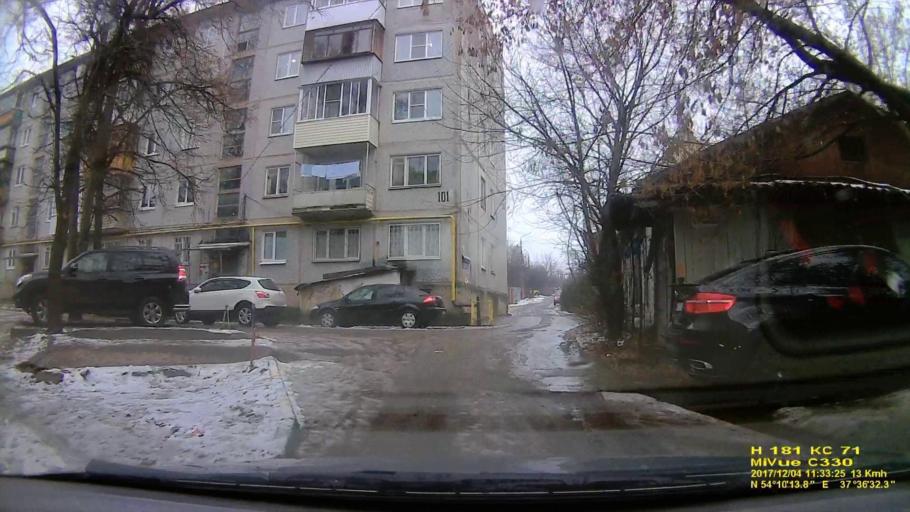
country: RU
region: Tula
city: Tula
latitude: 54.1704
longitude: 37.6096
